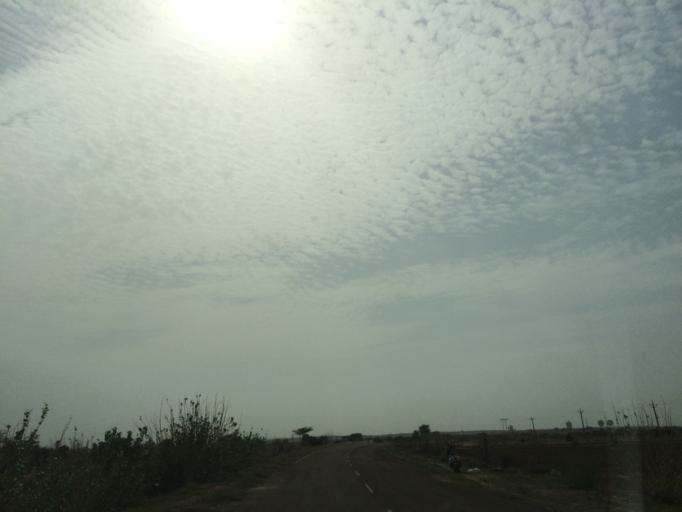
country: IN
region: Rajasthan
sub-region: Jaisalmer
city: Jaisalmer
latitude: 26.8757
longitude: 70.8839
